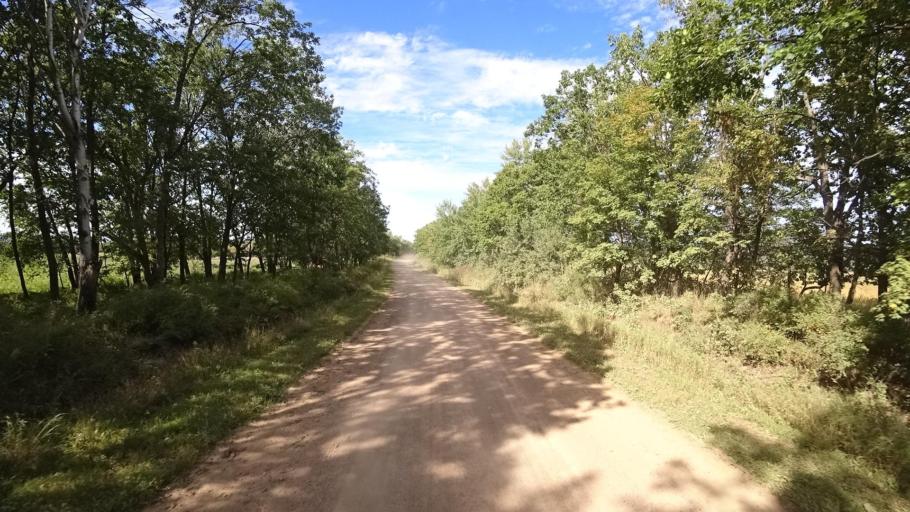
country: RU
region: Primorskiy
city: Yakovlevka
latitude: 44.4173
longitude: 133.5711
